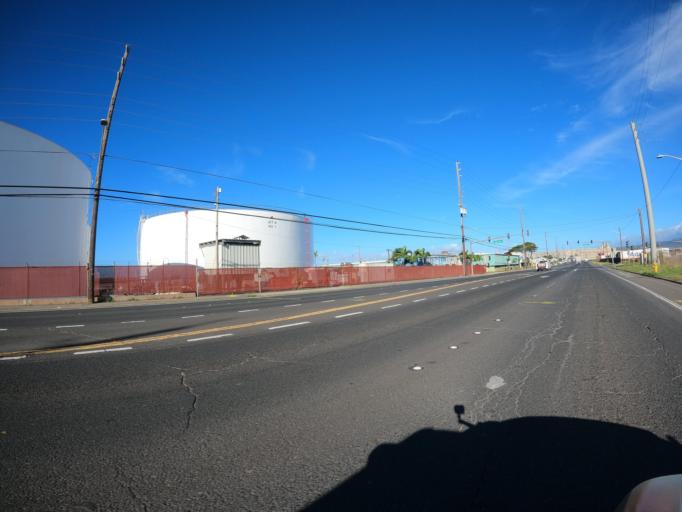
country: US
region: Hawaii
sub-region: Honolulu County
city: Honolulu
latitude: 21.3190
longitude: -157.8903
